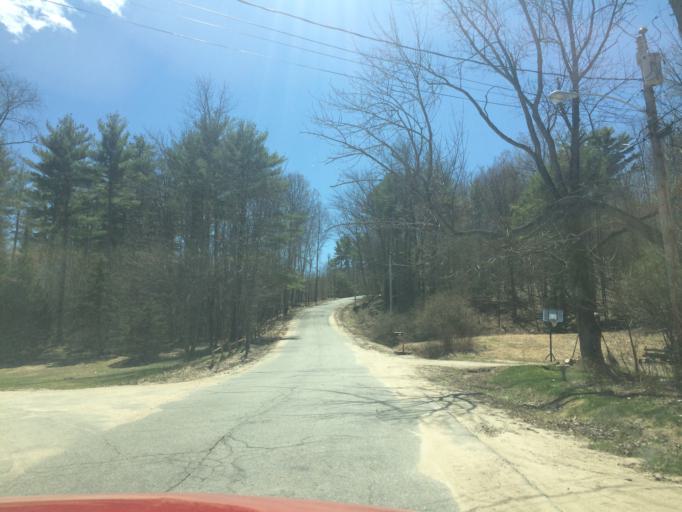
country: US
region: Maine
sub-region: Oxford County
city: Porter
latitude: 43.8048
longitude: -70.8742
